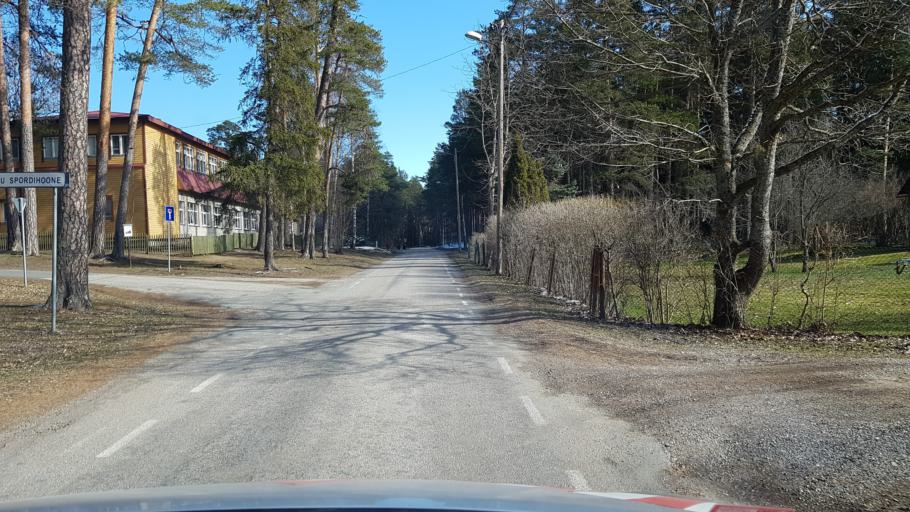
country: EE
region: Harju
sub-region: Loksa linn
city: Loksa
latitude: 59.5776
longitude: 25.9727
